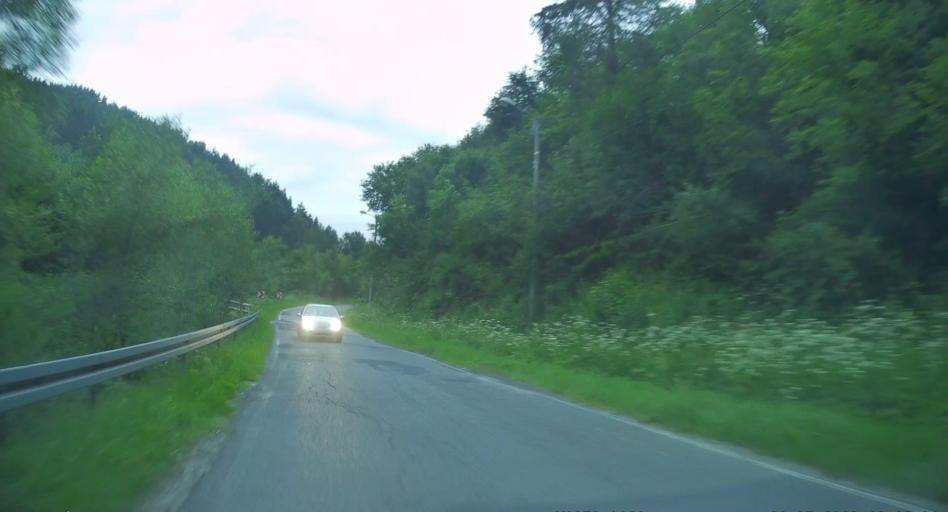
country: PL
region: Lesser Poland Voivodeship
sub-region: Powiat nowosadecki
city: Muszyna
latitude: 49.3715
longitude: 20.9233
